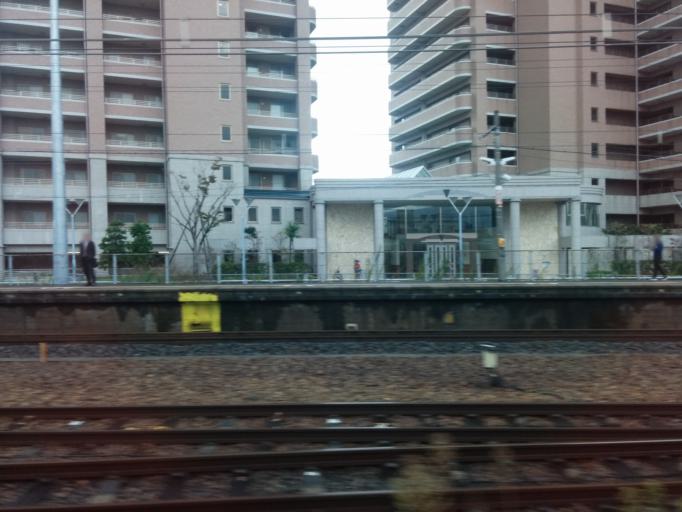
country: JP
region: Shiga Prefecture
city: Moriyama
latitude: 35.0694
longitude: 136.0236
